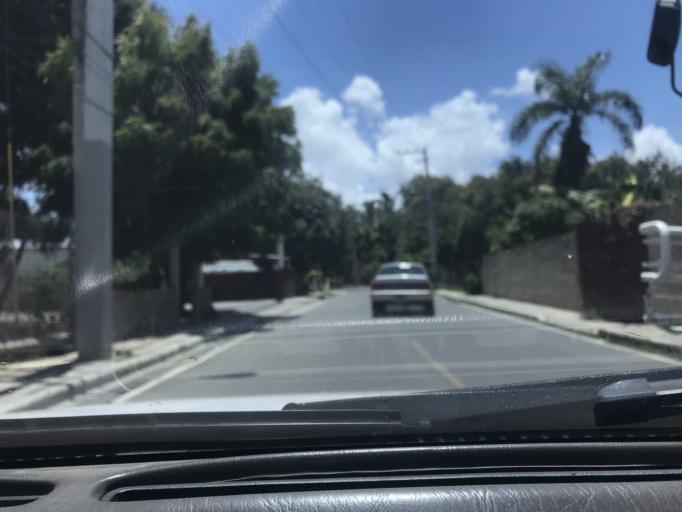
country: DO
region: Santiago
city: Santiago de los Caballeros
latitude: 19.4229
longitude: -70.7057
